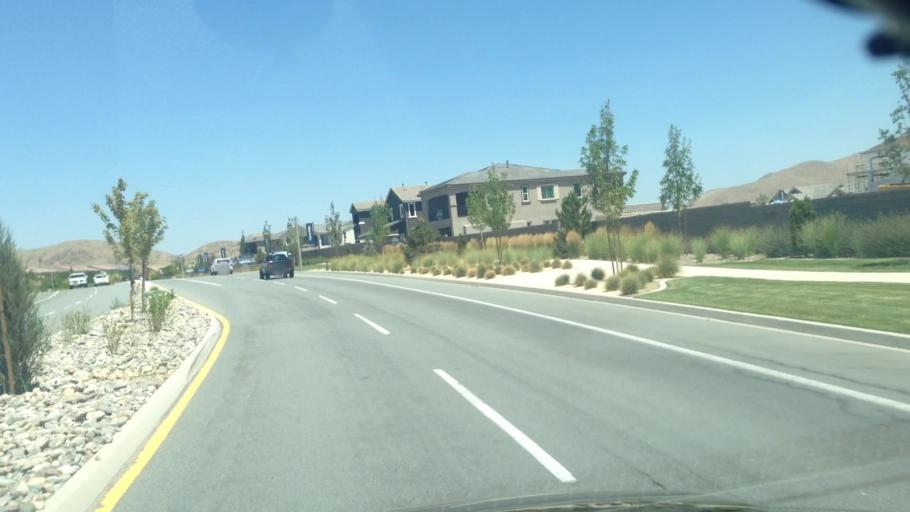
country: US
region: Nevada
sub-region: Washoe County
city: Sparks
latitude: 39.4454
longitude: -119.7270
